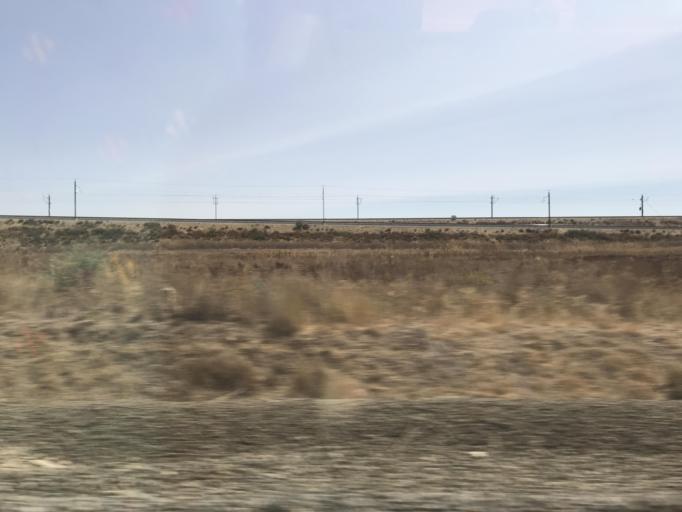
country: ES
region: Castille and Leon
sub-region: Provincia de Palencia
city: Venta de Banos
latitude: 41.9357
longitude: -4.4750
